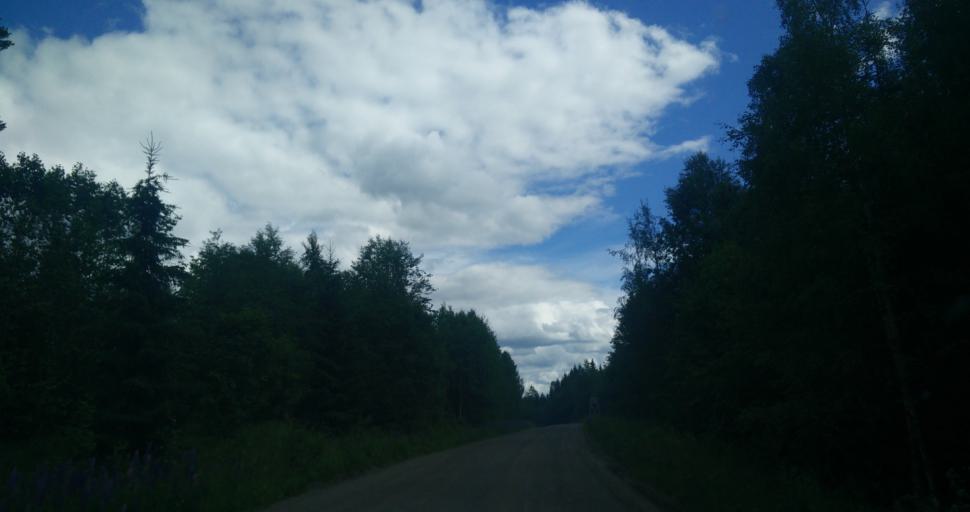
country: SE
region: Gaevleborg
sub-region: Nordanstigs Kommun
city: Bergsjoe
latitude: 62.0760
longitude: 16.7542
